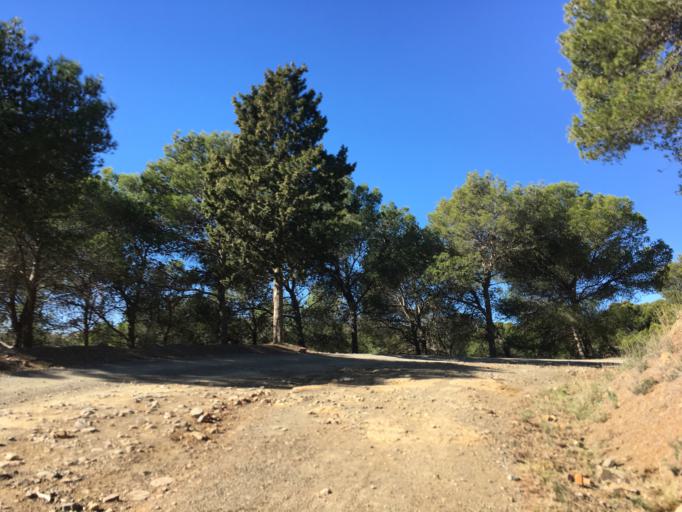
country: ES
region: Andalusia
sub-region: Provincia de Malaga
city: Malaga
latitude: 36.7826
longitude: -4.3900
